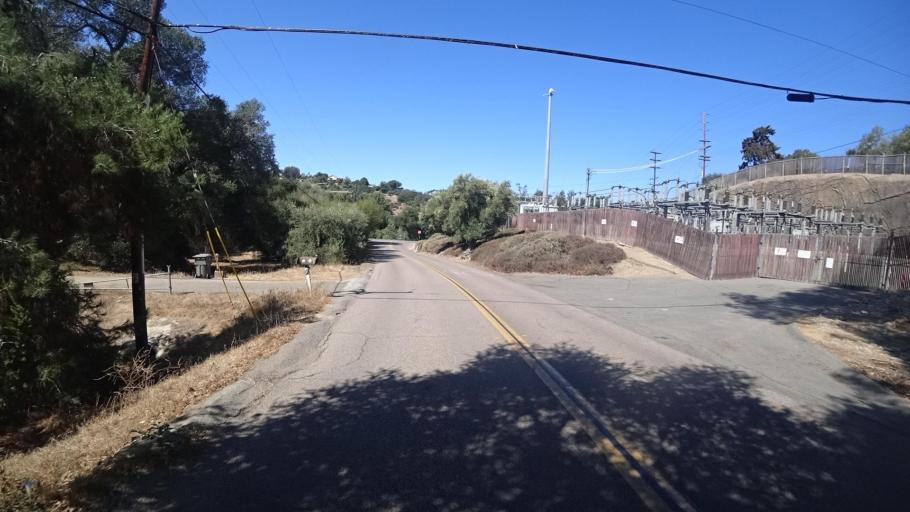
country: US
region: California
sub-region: San Diego County
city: Bonsall
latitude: 33.3288
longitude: -117.2350
